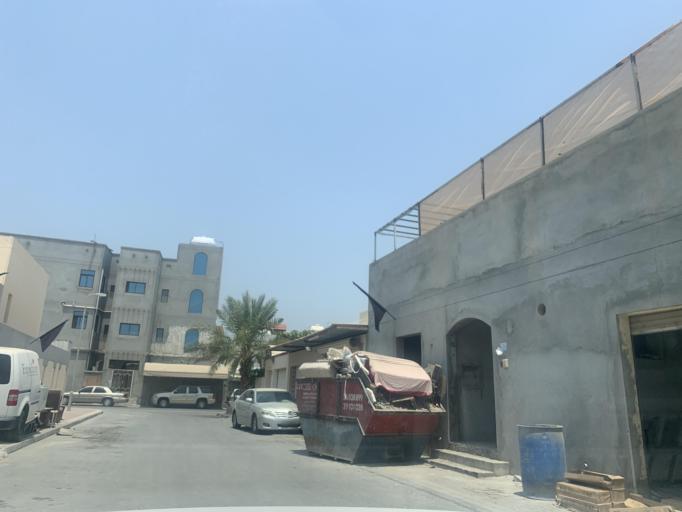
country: BH
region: Central Governorate
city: Madinat Hamad
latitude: 26.1418
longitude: 50.4628
